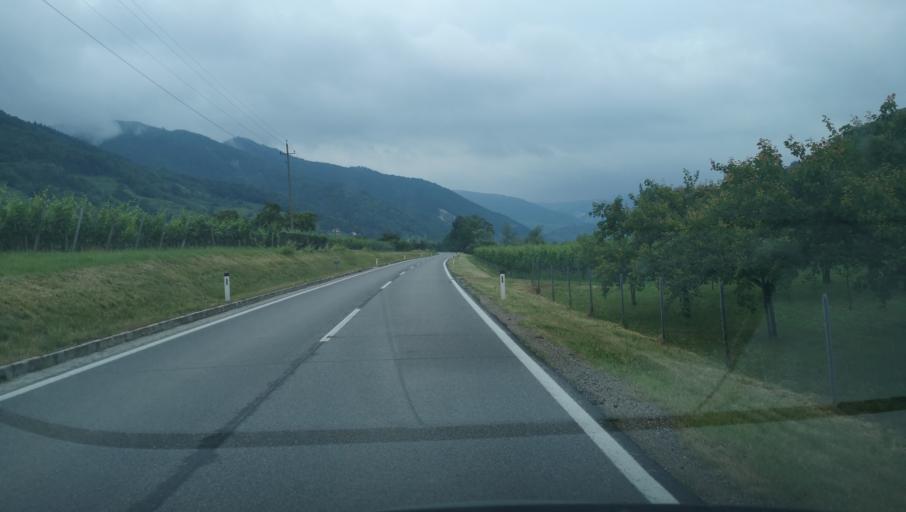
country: AT
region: Lower Austria
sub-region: Politischer Bezirk Krems
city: Aggsbach
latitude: 48.3270
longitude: 15.4065
